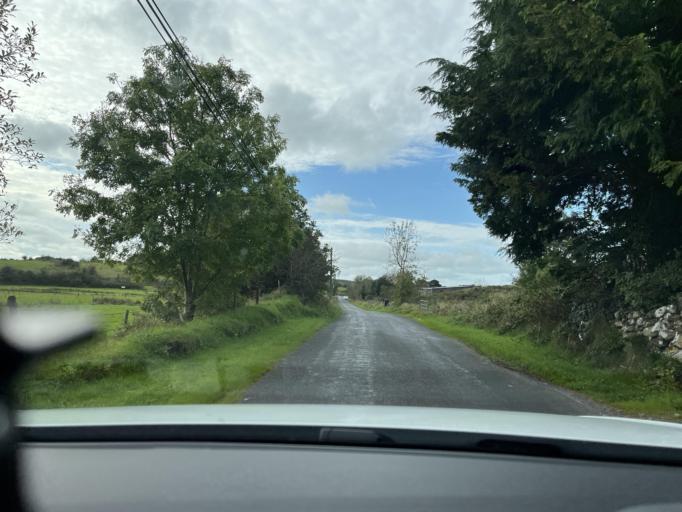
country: IE
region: Connaught
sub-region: Roscommon
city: Boyle
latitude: 54.0240
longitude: -8.3976
